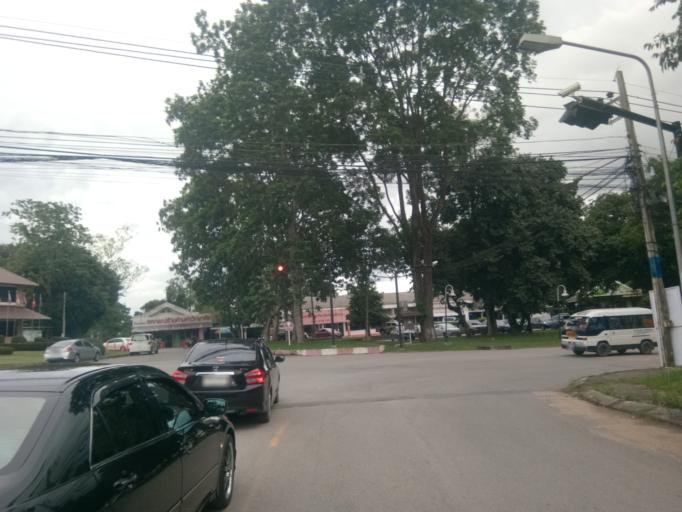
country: TH
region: Chiang Rai
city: Chiang Rai
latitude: 19.9827
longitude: 99.8515
